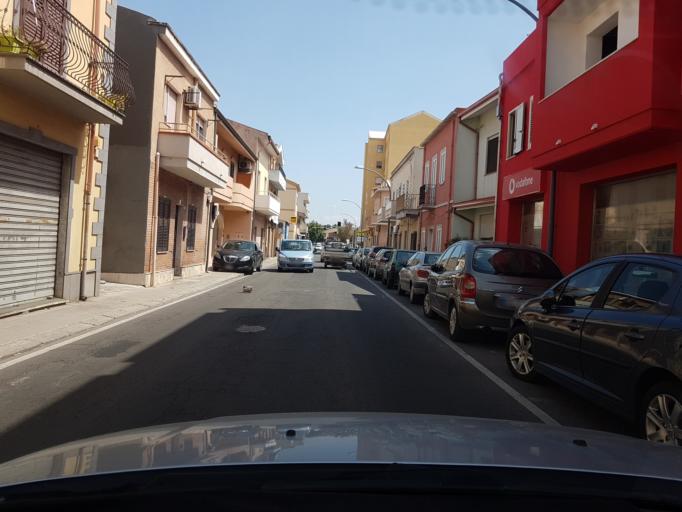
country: IT
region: Sardinia
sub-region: Provincia di Oristano
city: Oristano
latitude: 39.9067
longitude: 8.5979
